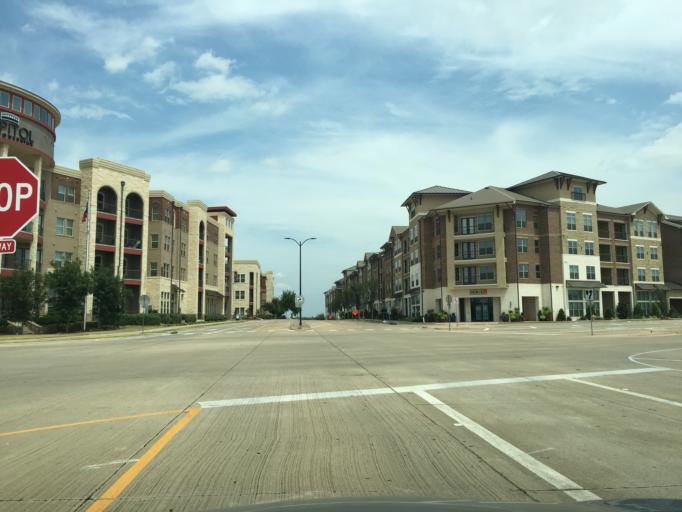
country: US
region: Texas
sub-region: Collin County
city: Frisco
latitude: 33.1053
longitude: -96.8009
